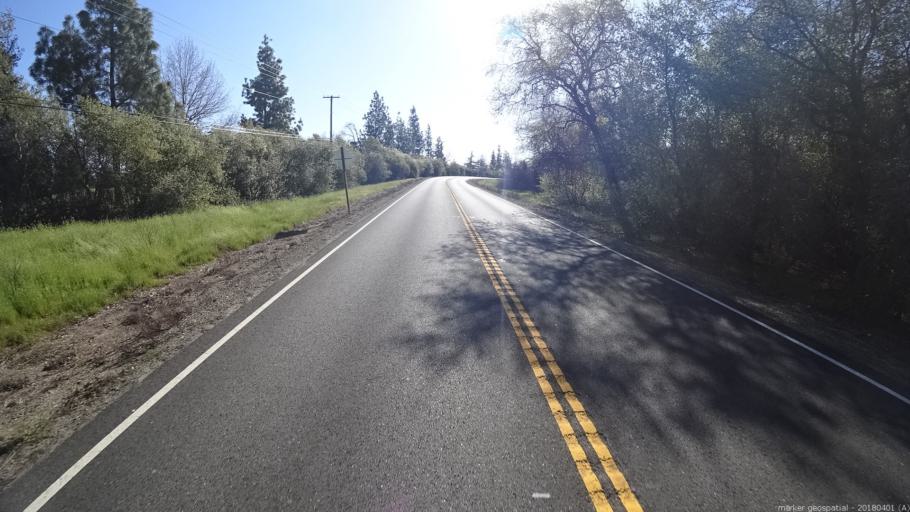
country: US
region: California
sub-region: Sacramento County
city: Rancho Murieta
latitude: 38.4905
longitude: -121.0885
